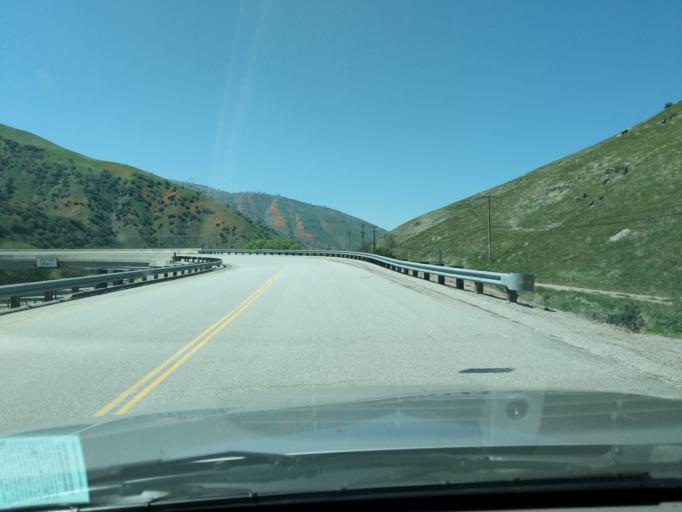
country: US
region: California
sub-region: Kern County
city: Lebec
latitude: 34.8770
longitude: -118.8935
